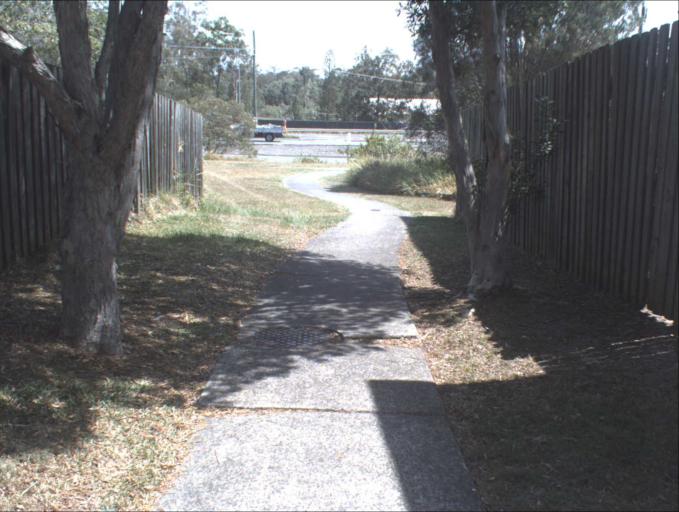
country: AU
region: Queensland
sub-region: Logan
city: Beenleigh
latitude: -27.6701
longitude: 153.1945
